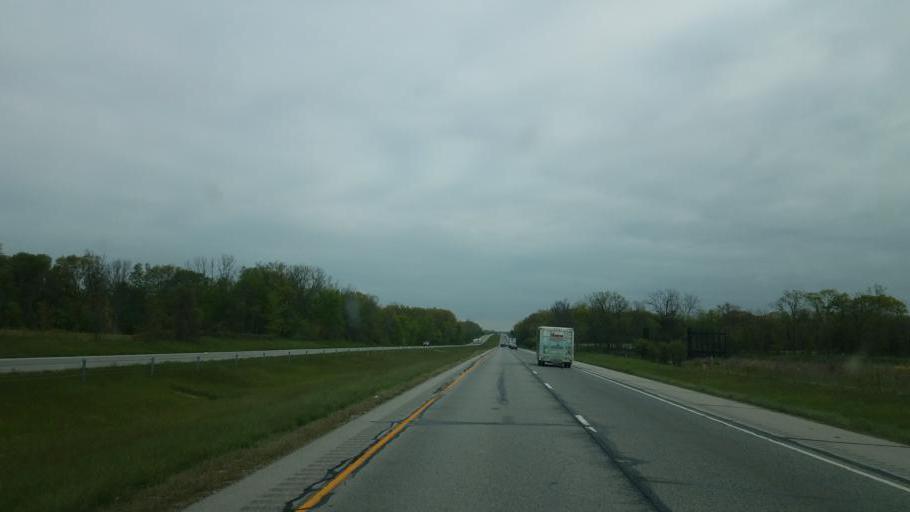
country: US
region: Indiana
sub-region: Allen County
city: Leo-Cedarville
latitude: 41.2674
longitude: -85.0868
